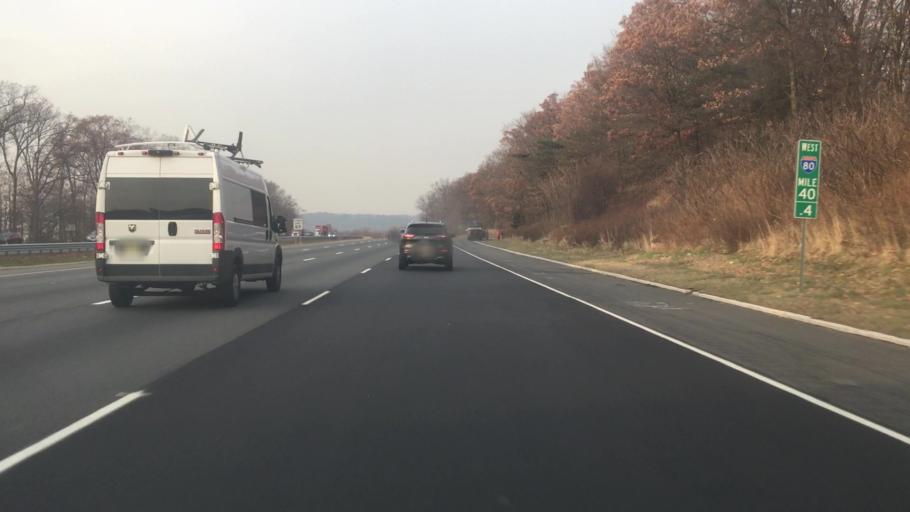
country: US
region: New Jersey
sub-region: Morris County
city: Mountain Lakes
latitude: 40.8810
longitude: -74.4689
